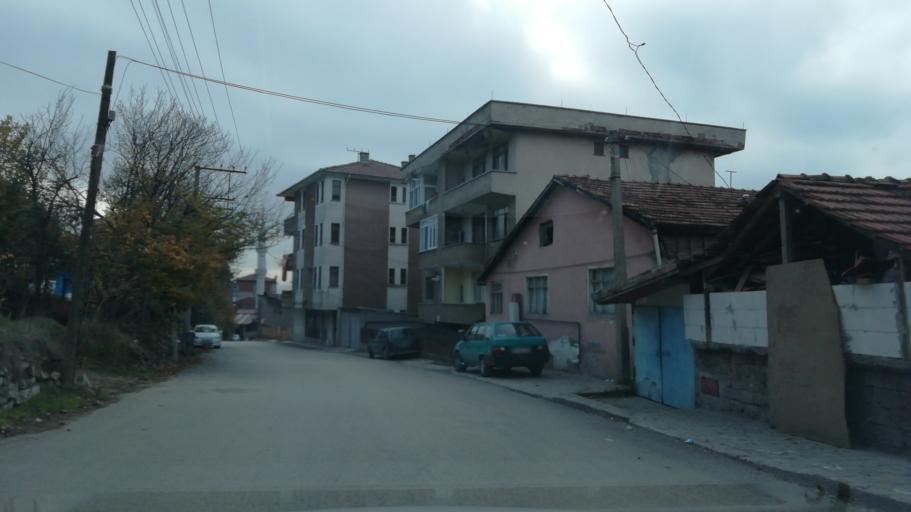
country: TR
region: Karabuk
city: Karabuk
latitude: 41.2171
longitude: 32.6283
